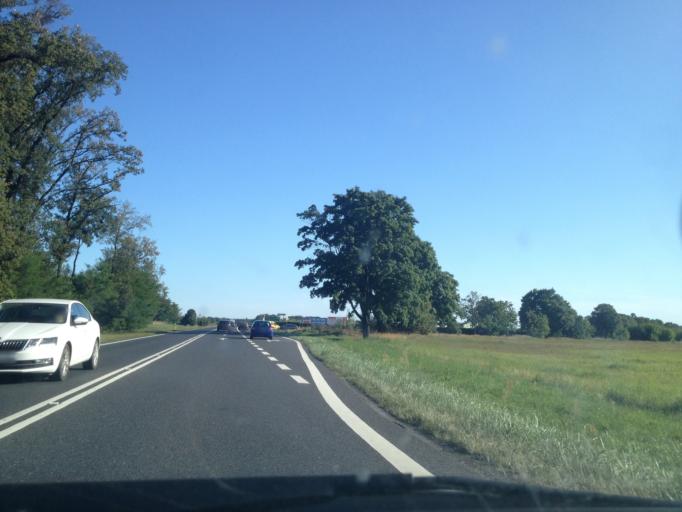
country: PL
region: Greater Poland Voivodeship
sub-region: Powiat sremski
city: Srem
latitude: 52.1335
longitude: 17.0416
